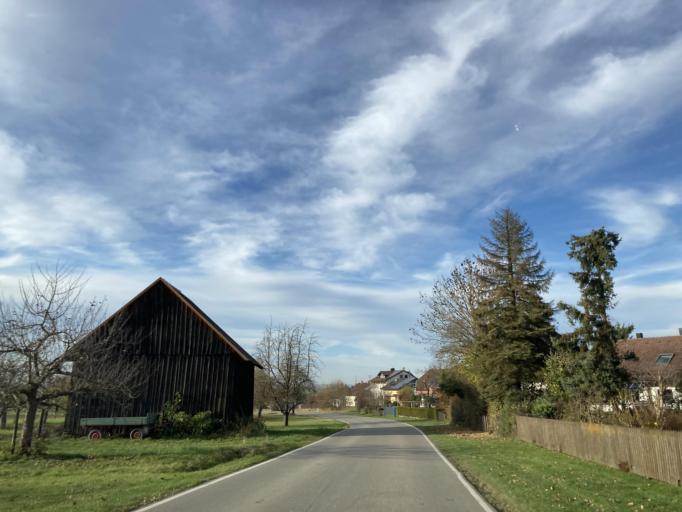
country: DE
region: Baden-Wuerttemberg
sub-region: Regierungsbezirk Stuttgart
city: Bondorf
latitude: 48.4740
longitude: 8.8149
